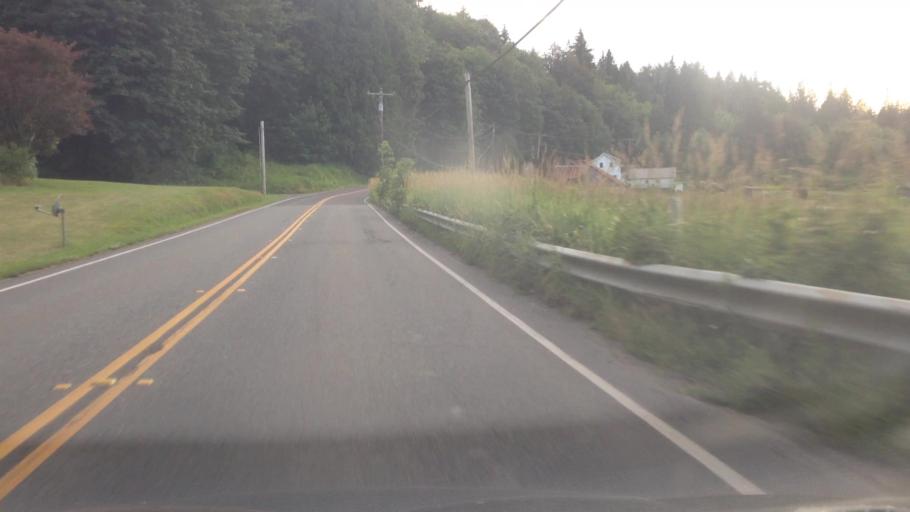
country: US
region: Washington
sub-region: King County
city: Duvall
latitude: 47.7429
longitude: -121.9442
